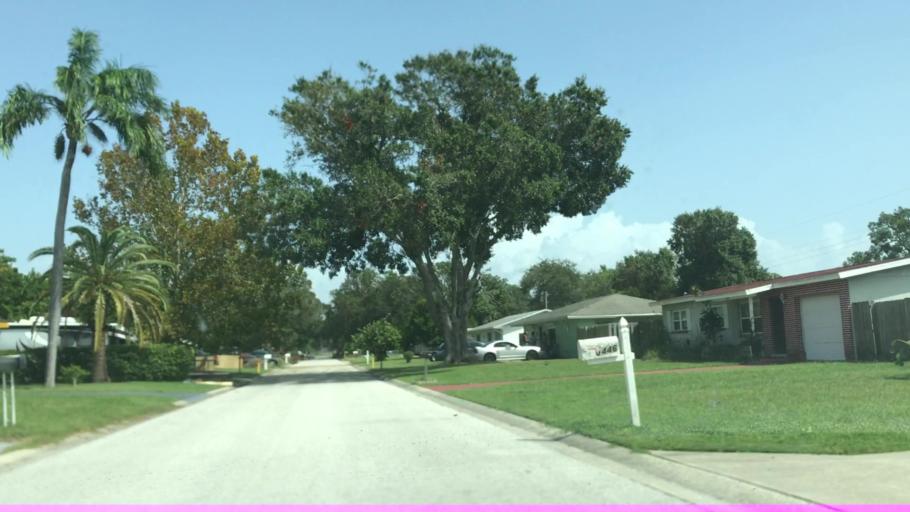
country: US
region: Florida
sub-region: Pinellas County
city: Kenneth City
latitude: 27.8243
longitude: -82.7074
